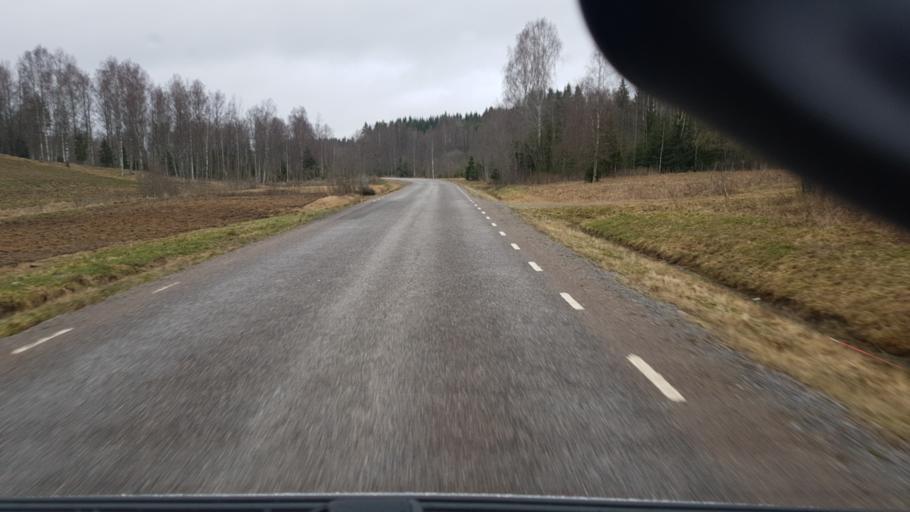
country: SE
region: Vaermland
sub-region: Eda Kommun
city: Charlottenberg
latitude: 59.9895
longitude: 12.3938
